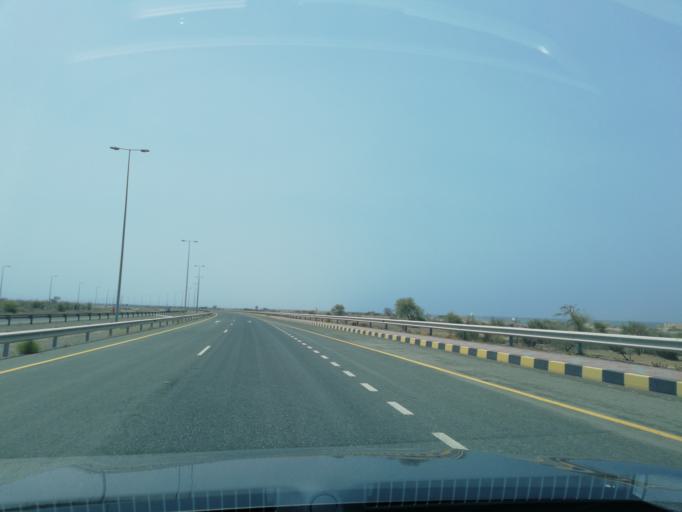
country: OM
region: Al Batinah
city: Shinas
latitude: 24.6585
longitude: 56.5113
